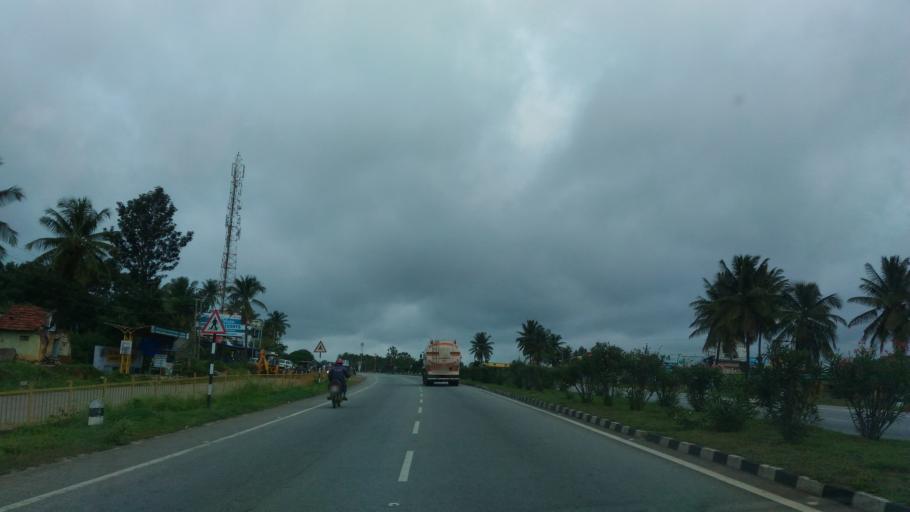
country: IN
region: Karnataka
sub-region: Bangalore Rural
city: Nelamangala
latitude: 13.0664
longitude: 77.3212
